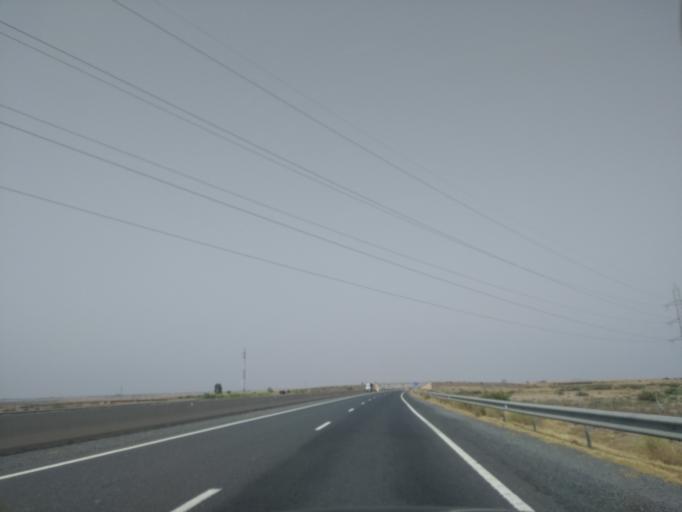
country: MA
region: Marrakech-Tensift-Al Haouz
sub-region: Marrakech
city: Marrakesh
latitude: 31.7557
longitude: -8.1912
